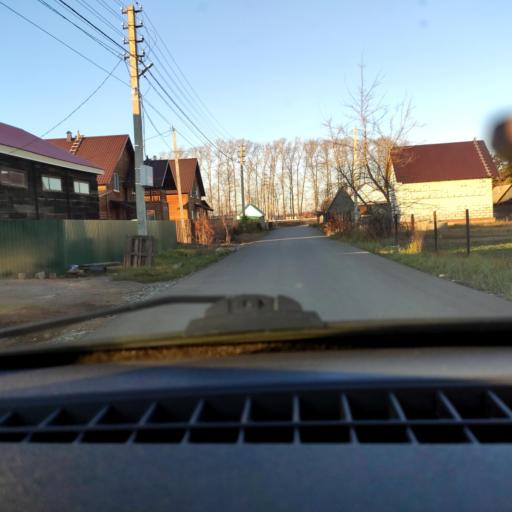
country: RU
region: Bashkortostan
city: Ufa
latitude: 54.6103
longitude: 55.8887
